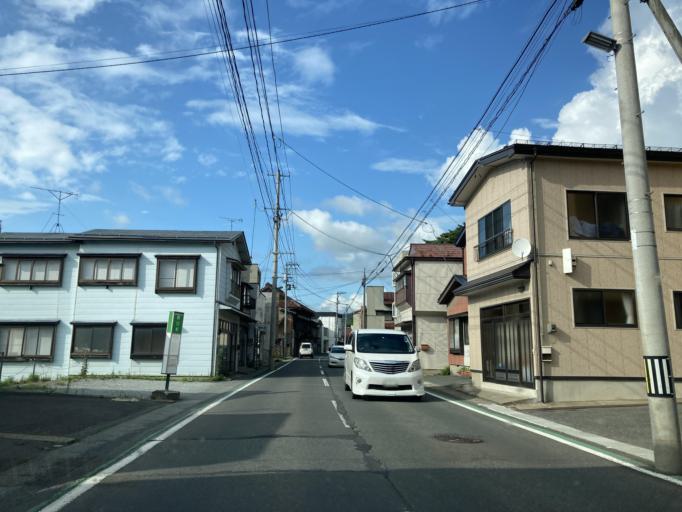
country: JP
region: Iwate
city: Ichinohe
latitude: 39.9690
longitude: 141.2215
